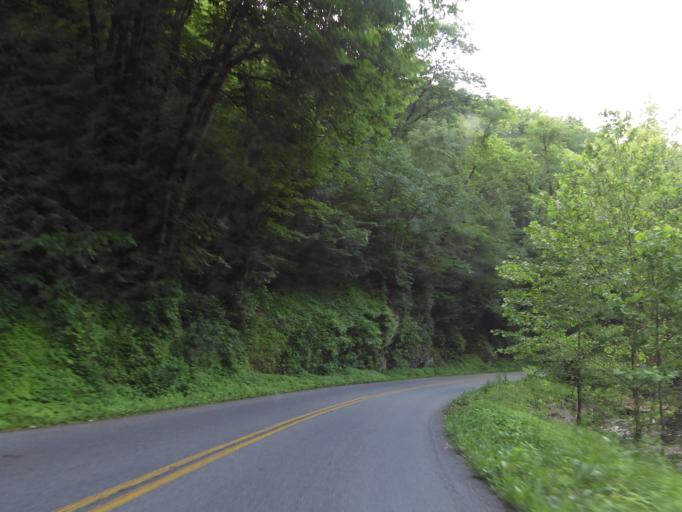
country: US
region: Tennessee
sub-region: Sevier County
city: Pigeon Forge
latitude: 35.6648
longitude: -83.6899
